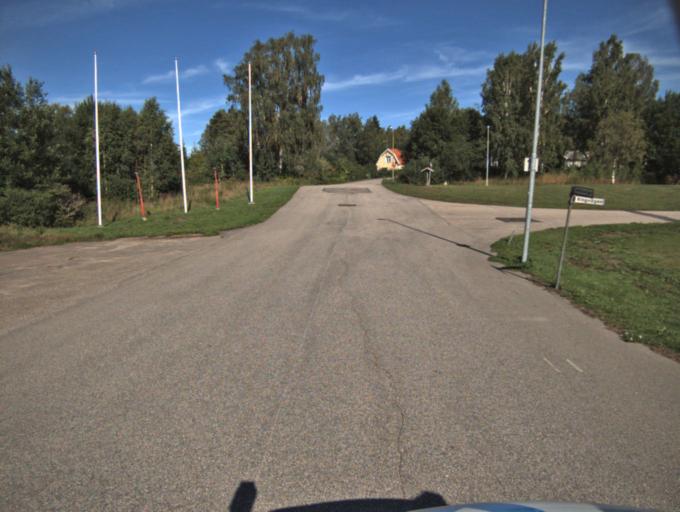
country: SE
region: Vaestra Goetaland
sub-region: Ulricehamns Kommun
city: Ulricehamn
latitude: 57.8997
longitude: 13.4596
